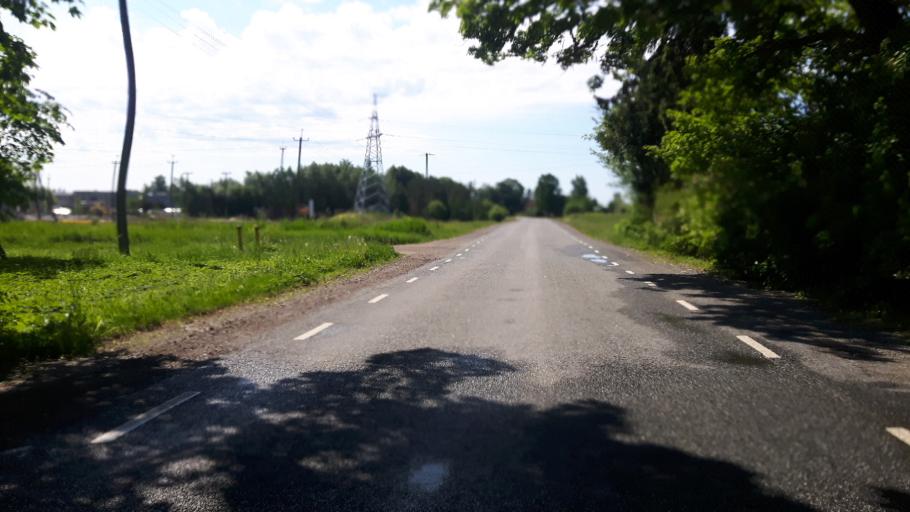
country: EE
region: Paernumaa
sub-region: Vaendra vald (alev)
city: Vandra
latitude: 58.6594
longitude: 25.0237
